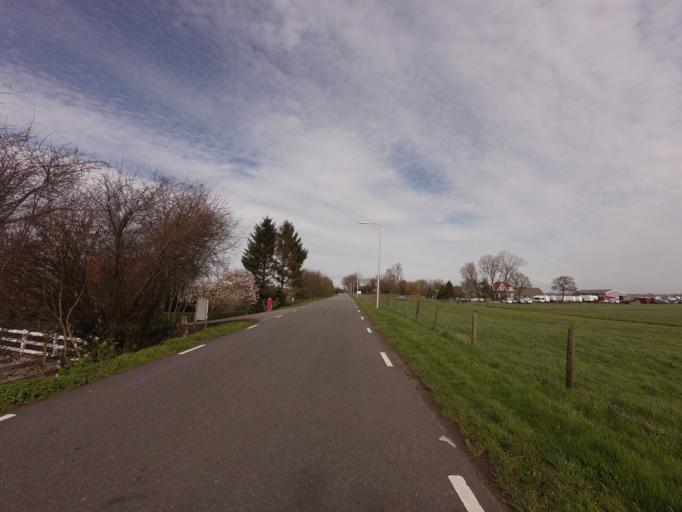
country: NL
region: North Holland
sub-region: Gemeente Uithoorn
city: Uithoorn
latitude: 52.2568
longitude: 4.8376
